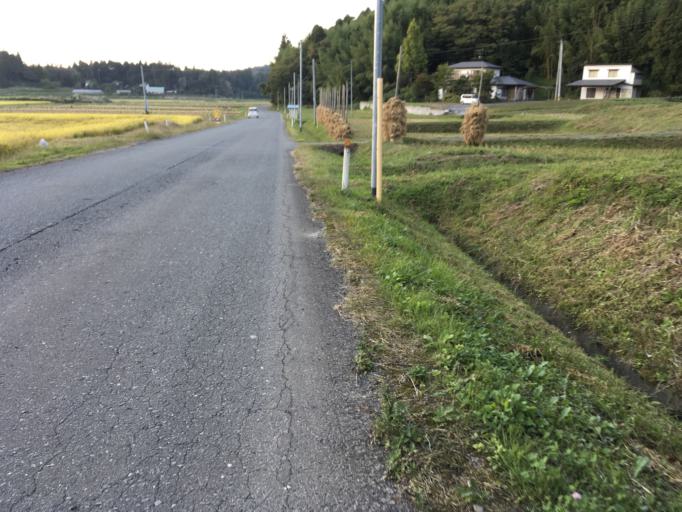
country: JP
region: Iwate
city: Ichinoseki
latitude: 38.7819
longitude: 141.2426
